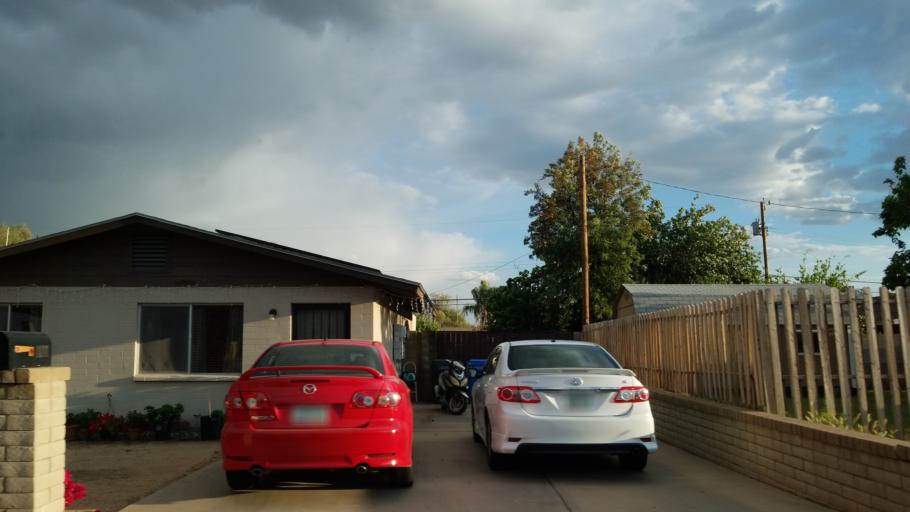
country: US
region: Arizona
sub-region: Maricopa County
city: Paradise Valley
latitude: 33.5911
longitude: -112.0498
